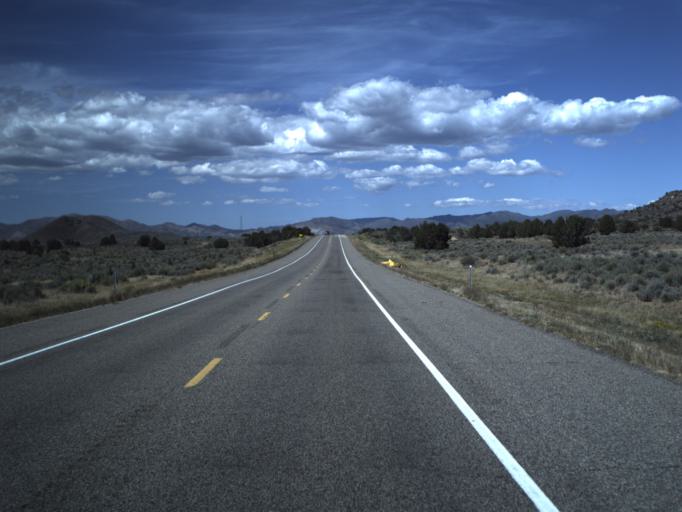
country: US
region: Utah
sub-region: Washington County
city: Ivins
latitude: 37.2833
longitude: -113.6547
